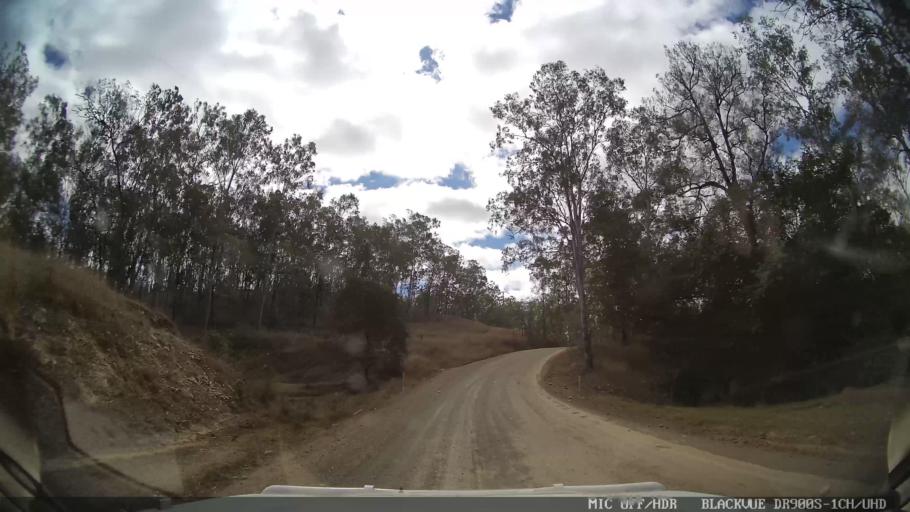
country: AU
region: Queensland
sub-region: Gladstone
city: Toolooa
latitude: -24.5531
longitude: 151.3363
